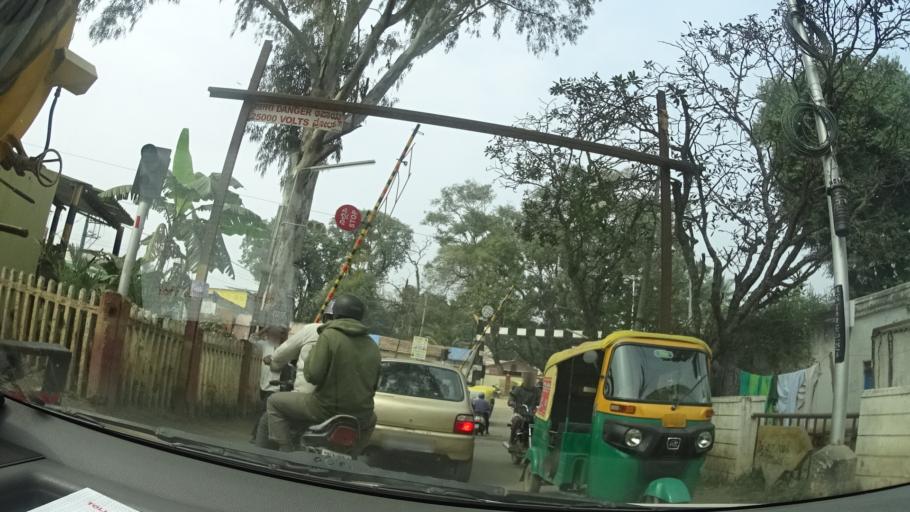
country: IN
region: Karnataka
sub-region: Bangalore Urban
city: Bangalore
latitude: 13.0211
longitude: 77.6236
